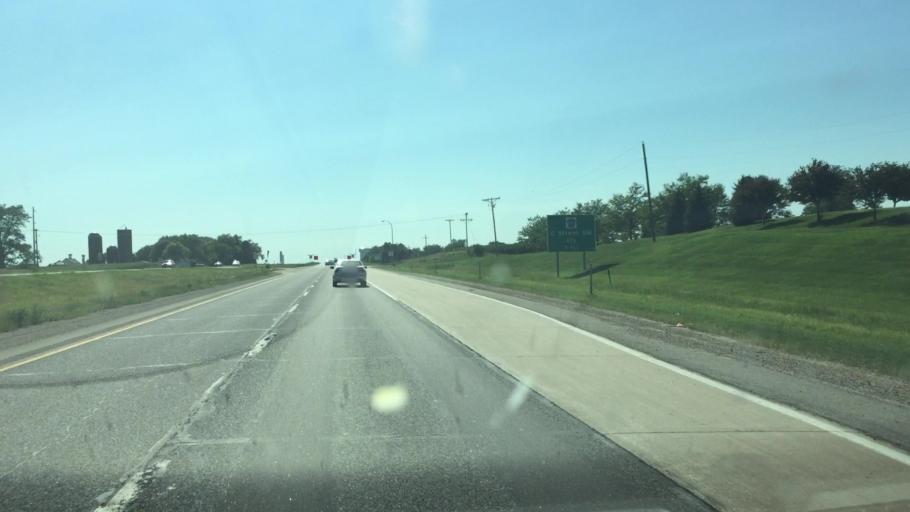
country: US
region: Iowa
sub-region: Linn County
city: Ely
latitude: 41.9264
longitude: -91.6158
